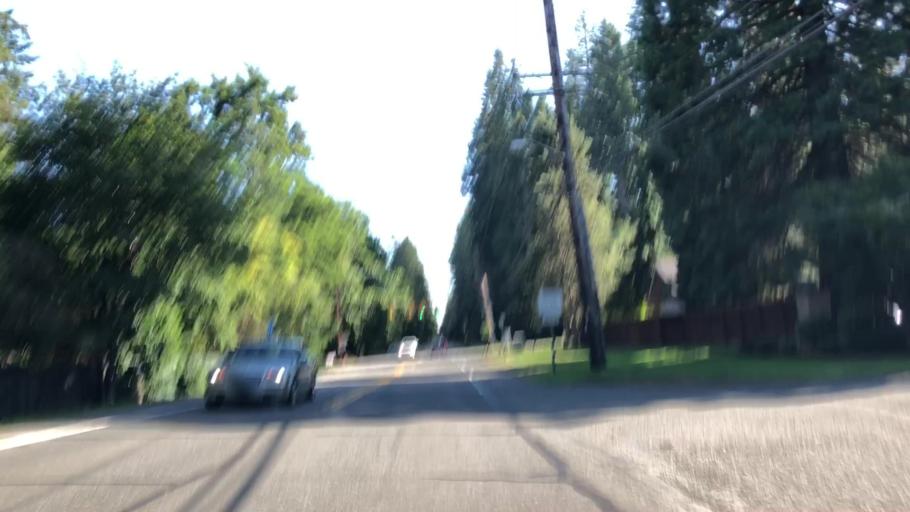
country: US
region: Washington
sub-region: King County
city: Cottage Lake
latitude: 47.7390
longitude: -122.0791
